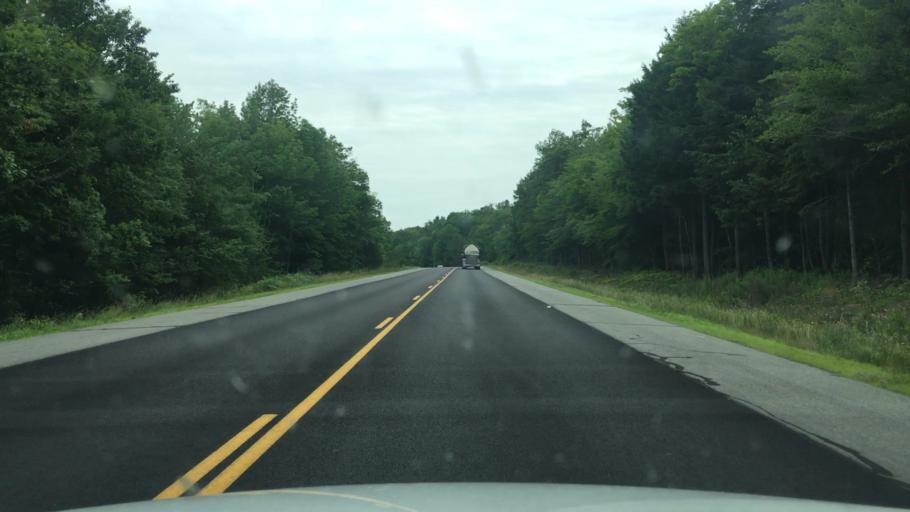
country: US
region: Maine
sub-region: Knox County
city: Washington
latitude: 44.3810
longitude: -69.3680
